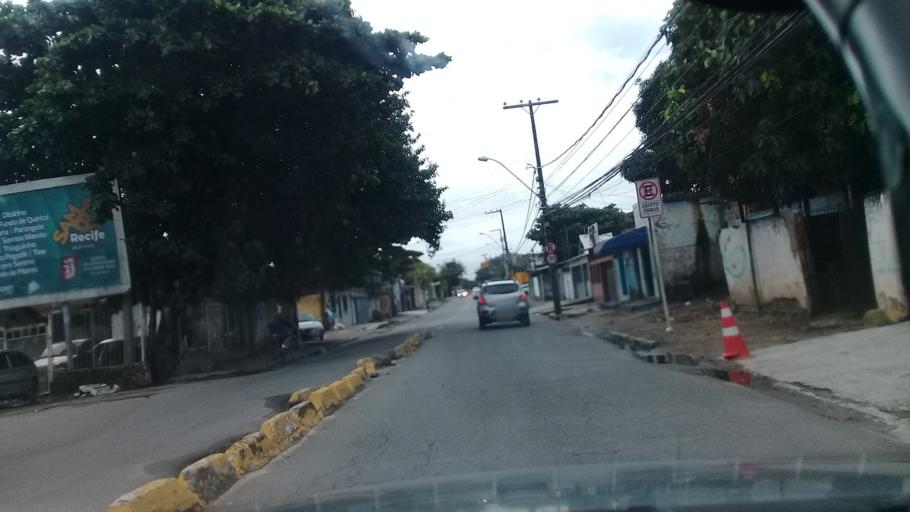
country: BR
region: Pernambuco
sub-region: Recife
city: Recife
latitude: -8.0383
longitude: -34.8794
